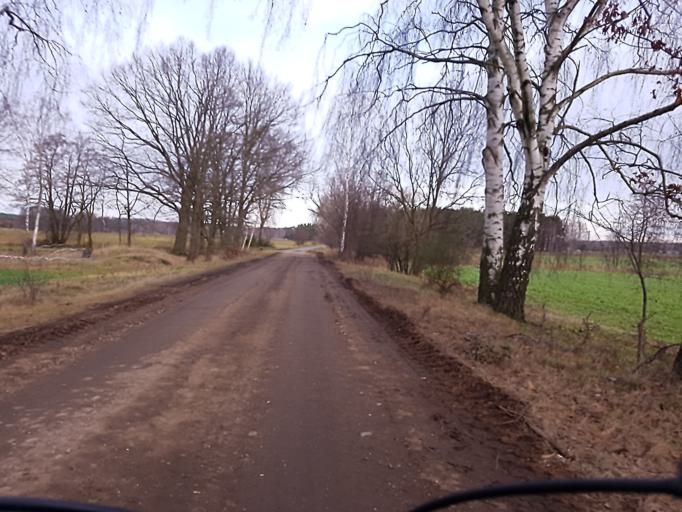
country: DE
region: Brandenburg
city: Schilda
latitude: 51.5707
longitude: 13.3923
